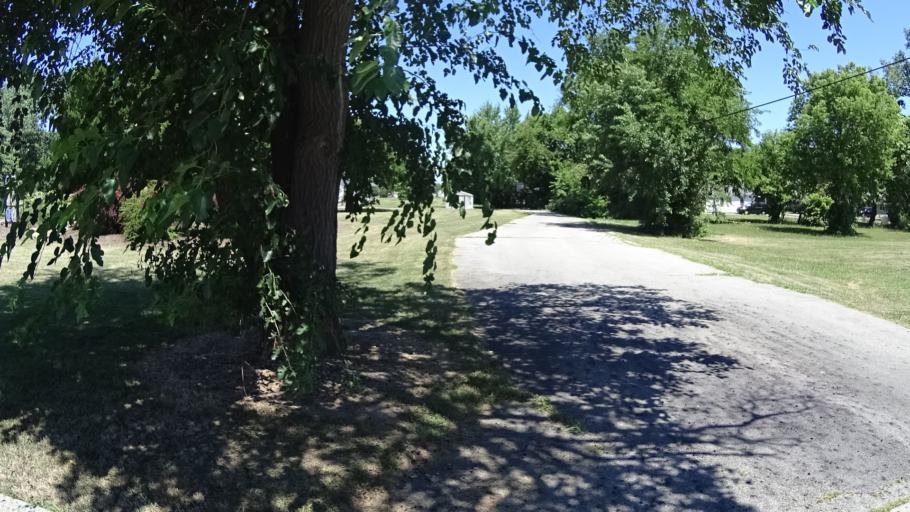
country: US
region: Ohio
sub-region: Erie County
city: Sandusky
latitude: 41.4398
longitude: -82.6925
